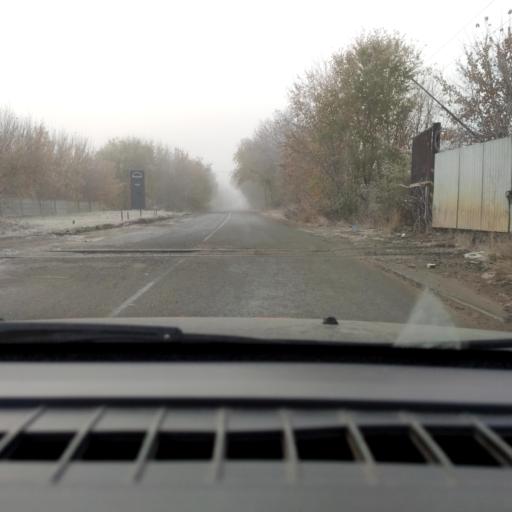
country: RU
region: Samara
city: Tol'yatti
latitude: 53.5852
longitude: 49.2572
